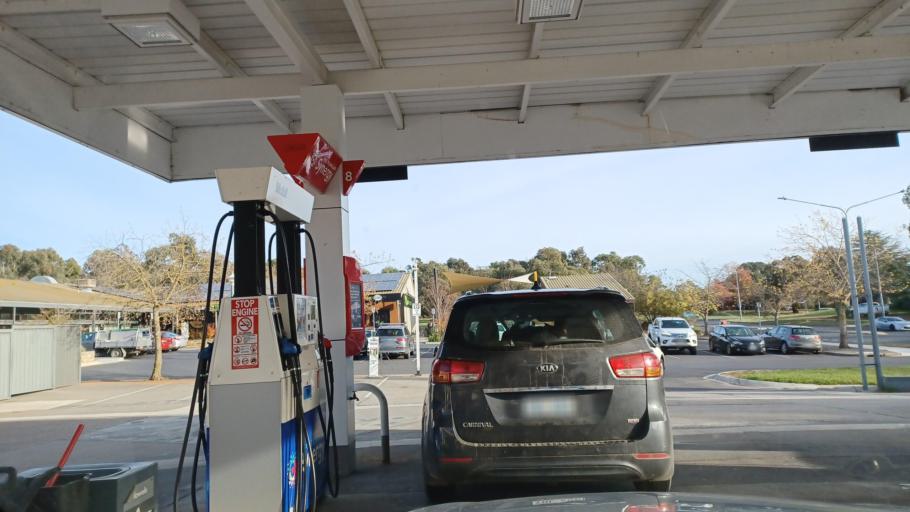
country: AU
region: Australian Capital Territory
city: Belconnen
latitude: -35.1948
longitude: 149.0624
